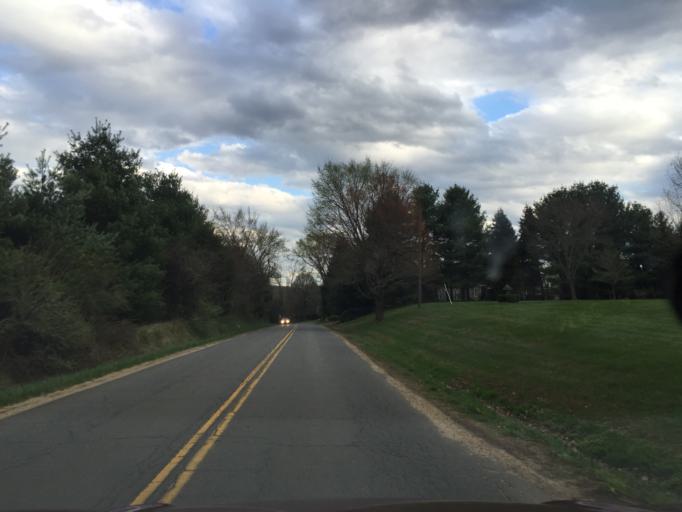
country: US
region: Maryland
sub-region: Frederick County
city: Point of Rocks
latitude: 39.2635
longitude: -77.5838
